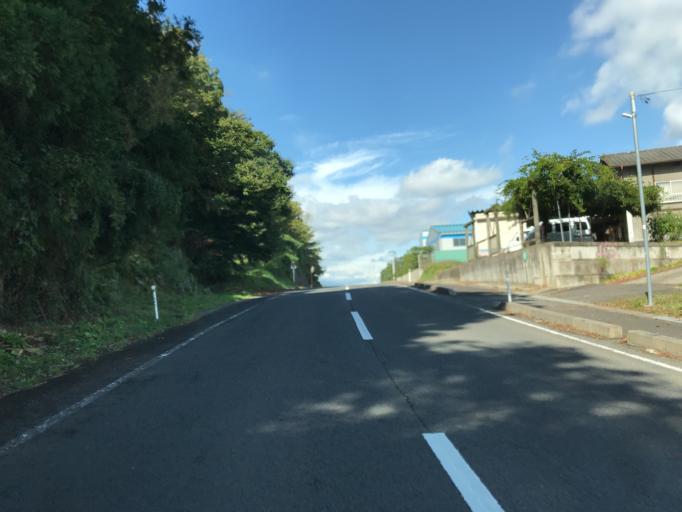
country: JP
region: Fukushima
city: Fukushima-shi
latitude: 37.6562
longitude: 140.5229
